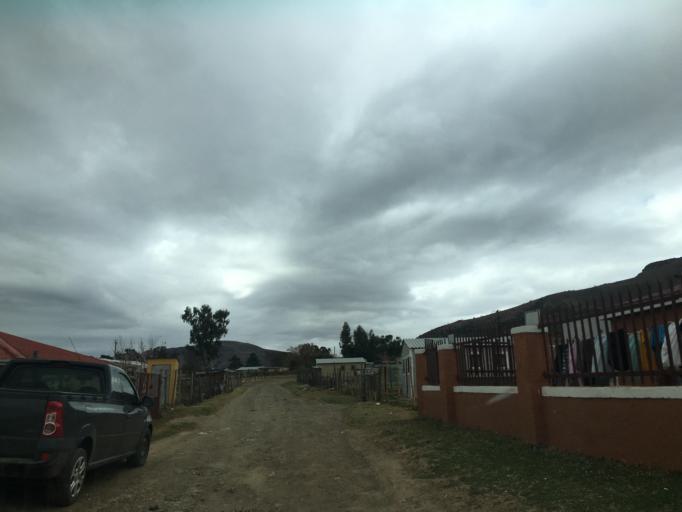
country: ZA
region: Eastern Cape
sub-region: Chris Hani District Municipality
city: Cala
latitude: -31.5322
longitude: 27.7012
